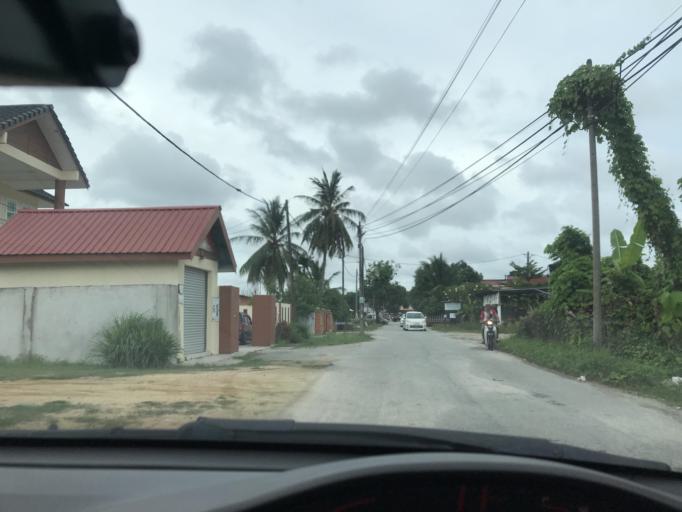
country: MY
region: Kelantan
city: Kota Bharu
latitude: 6.1168
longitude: 102.2201
